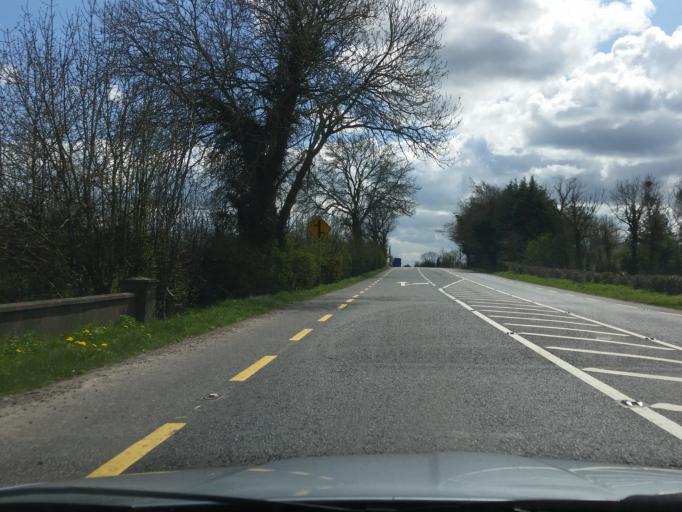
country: IE
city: Kentstown
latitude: 53.6679
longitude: -6.5312
